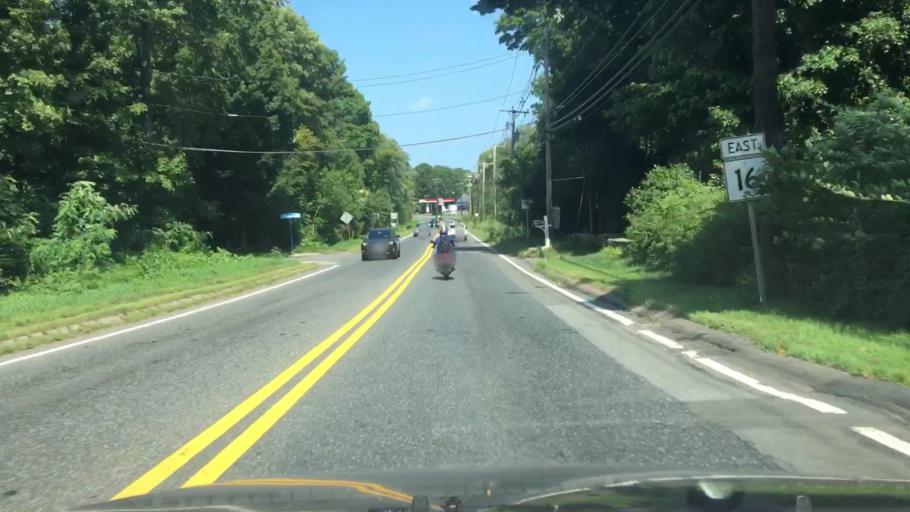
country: US
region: Massachusetts
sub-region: Middlesex County
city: Holliston
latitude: 42.1838
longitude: -71.4433
